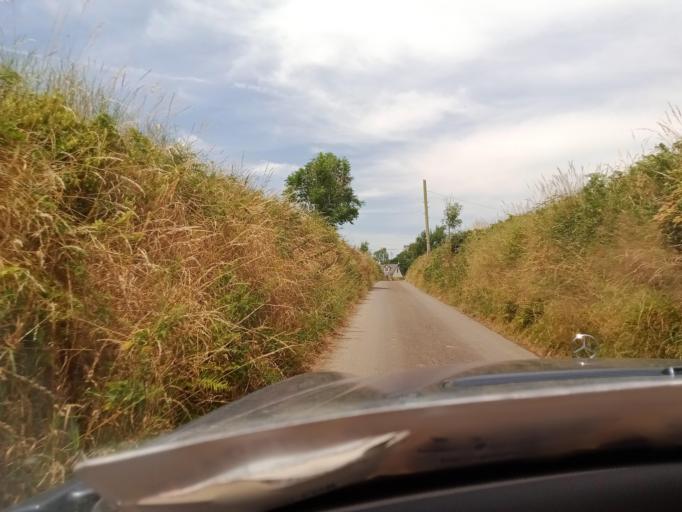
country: IE
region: Leinster
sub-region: Kilkenny
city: Mooncoin
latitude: 52.2506
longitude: -7.2141
